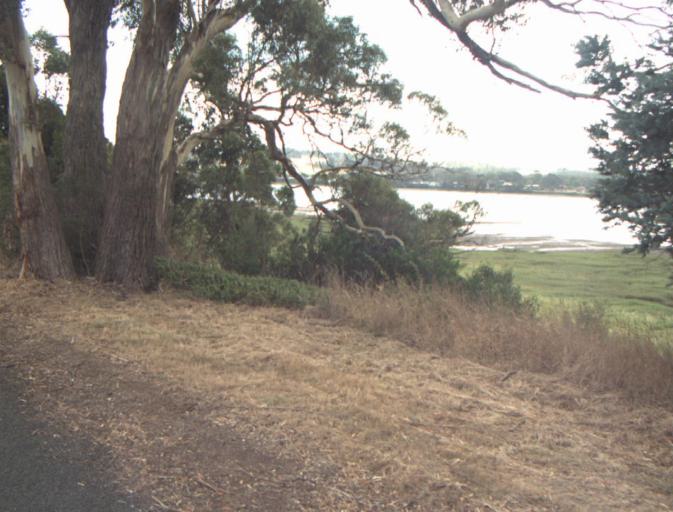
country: AU
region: Tasmania
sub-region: Launceston
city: Mayfield
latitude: -41.2877
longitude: 146.9957
